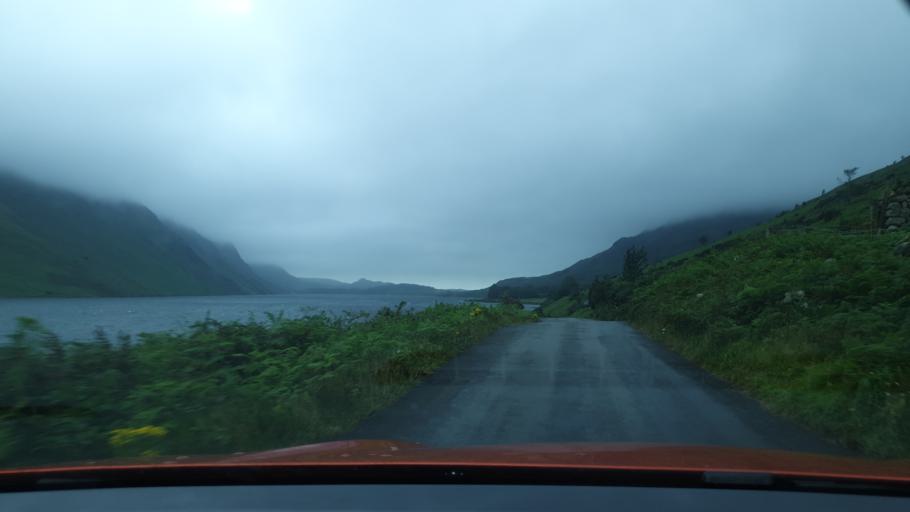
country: GB
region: England
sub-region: Cumbria
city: Keswick
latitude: 54.4544
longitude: -3.2713
